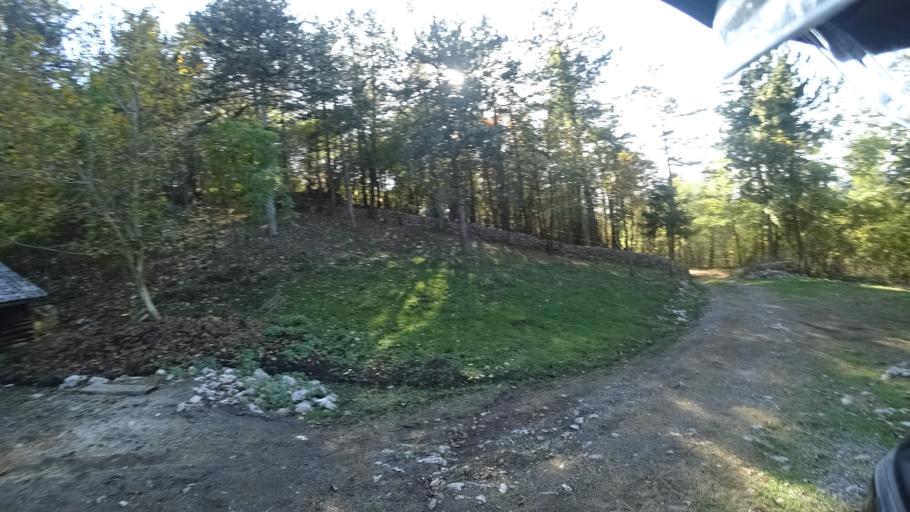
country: HR
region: Primorsko-Goranska
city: Klana
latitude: 45.4721
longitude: 14.3501
